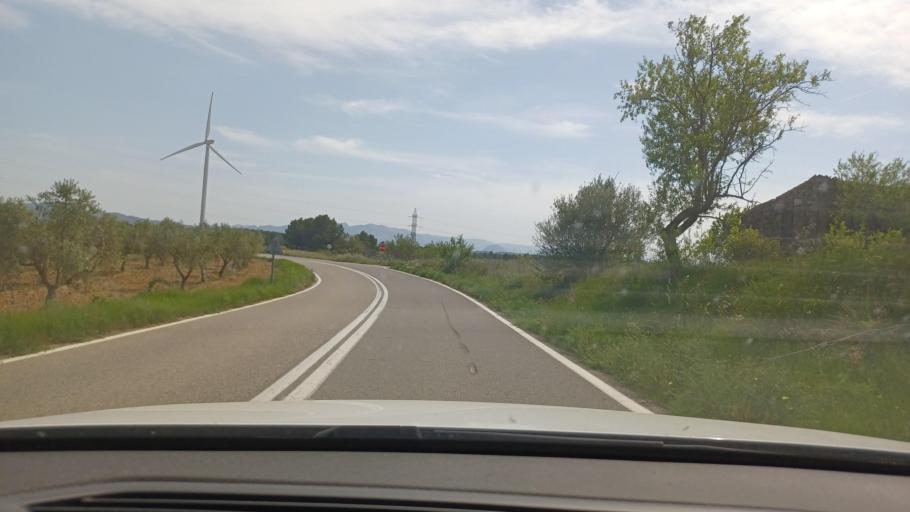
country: ES
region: Catalonia
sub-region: Provincia de Tarragona
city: Vilalba dels Arcs
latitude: 41.1016
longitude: 0.4169
